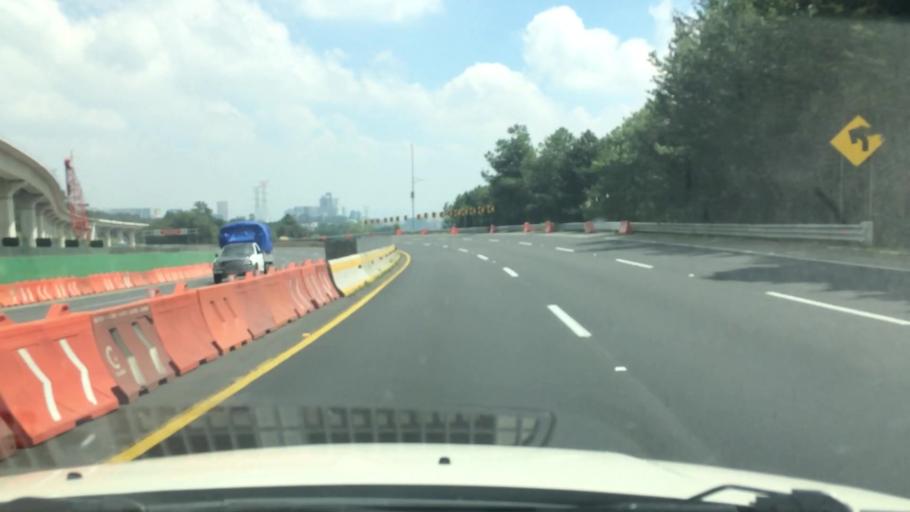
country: MX
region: Mexico City
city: Cuajimalpa
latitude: 19.3365
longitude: -99.2993
